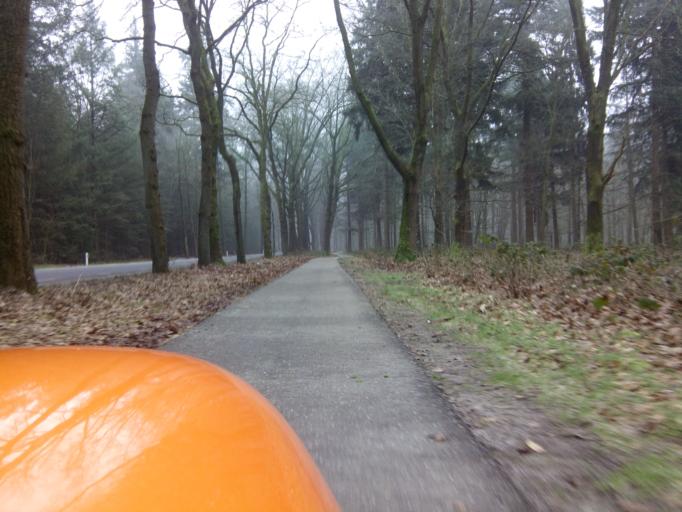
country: NL
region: Gelderland
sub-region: Gemeente Putten
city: Putten
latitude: 52.2446
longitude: 5.6427
